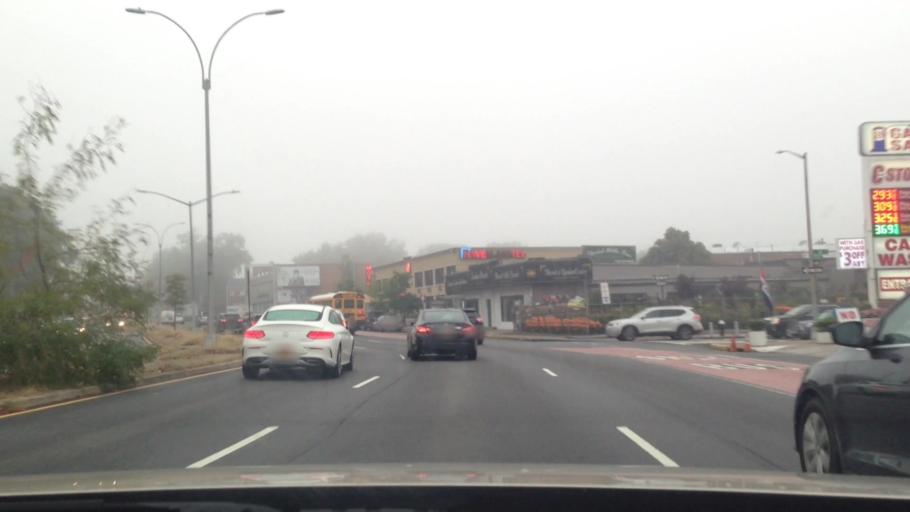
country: US
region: New York
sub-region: Queens County
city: Borough of Queens
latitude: 40.7146
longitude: -73.8598
